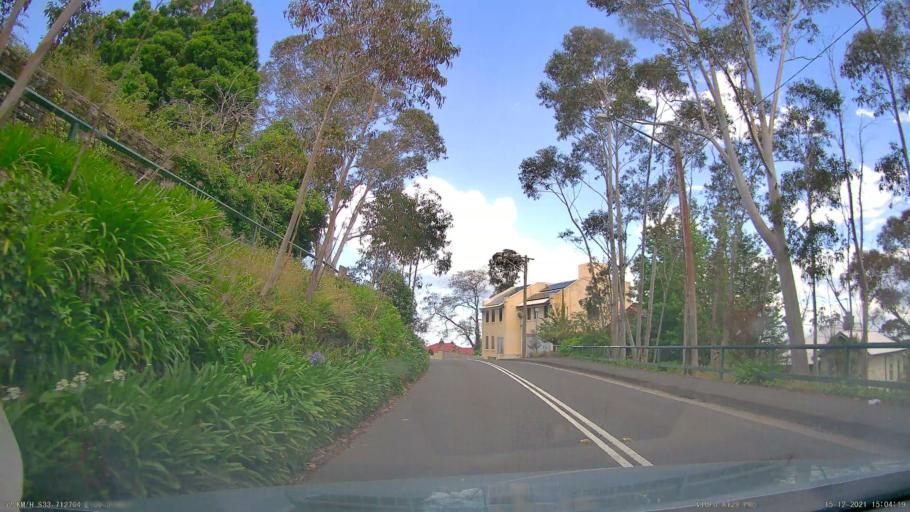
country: AU
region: New South Wales
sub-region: Blue Mountains Municipality
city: Katoomba
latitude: -33.7128
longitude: 150.3148
